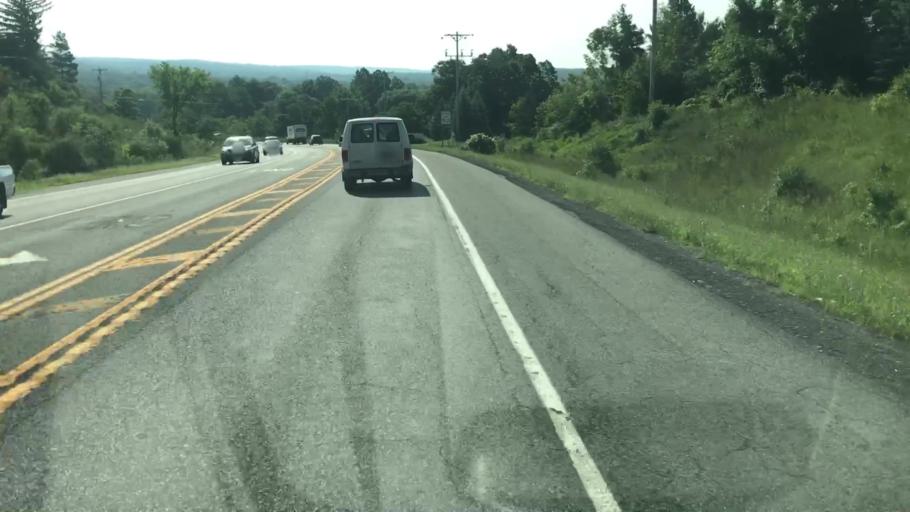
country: US
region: New York
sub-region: Onondaga County
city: Fayetteville
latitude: 43.0150
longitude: -76.0149
